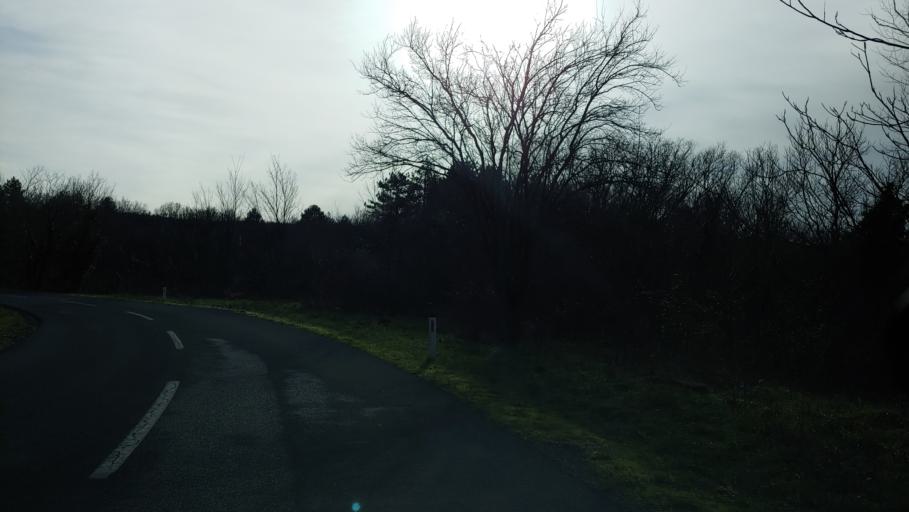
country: IT
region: Friuli Venezia Giulia
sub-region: Provincia di Trieste
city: Sistiana-Visogliano
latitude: 45.8112
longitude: 13.6455
